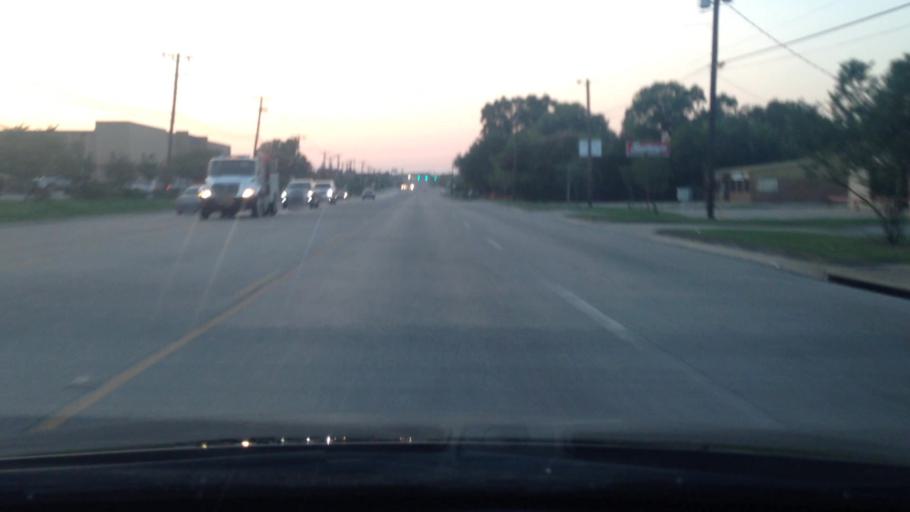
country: US
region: Texas
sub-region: Tarrant County
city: Kennedale
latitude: 32.6557
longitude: -97.2310
